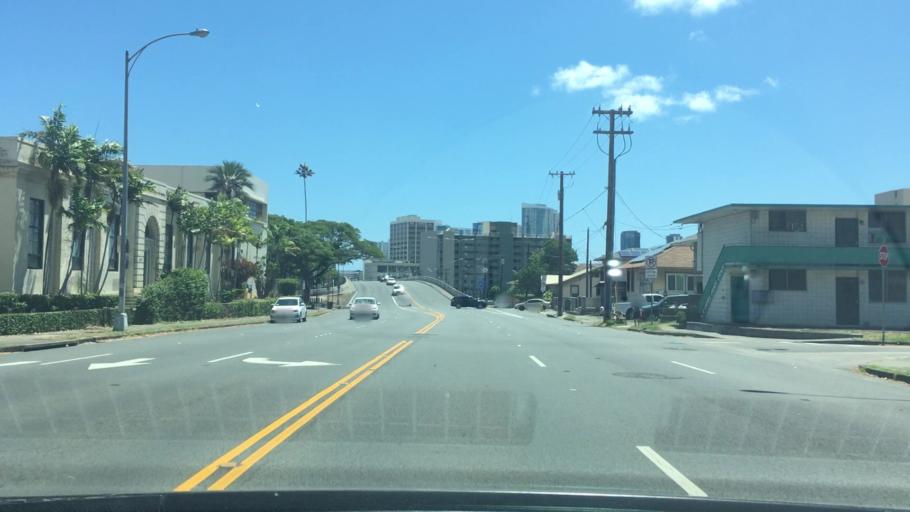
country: US
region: Hawaii
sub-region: Honolulu County
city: Honolulu
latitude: 21.3042
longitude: -157.8369
